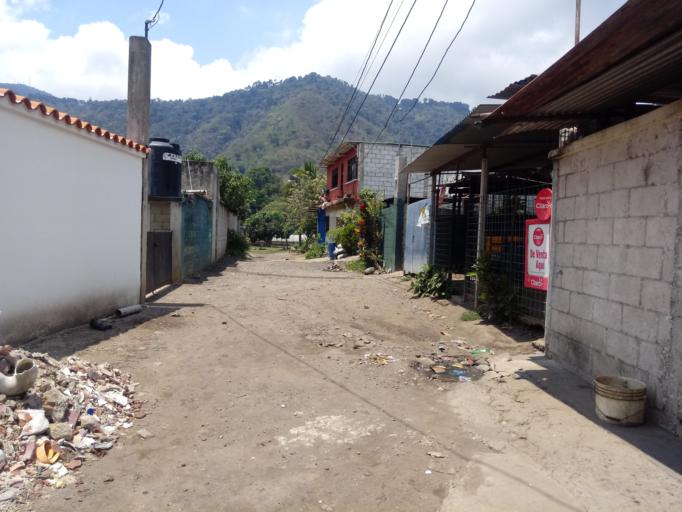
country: GT
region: Guatemala
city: Villa Canales
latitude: 14.4259
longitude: -90.5520
